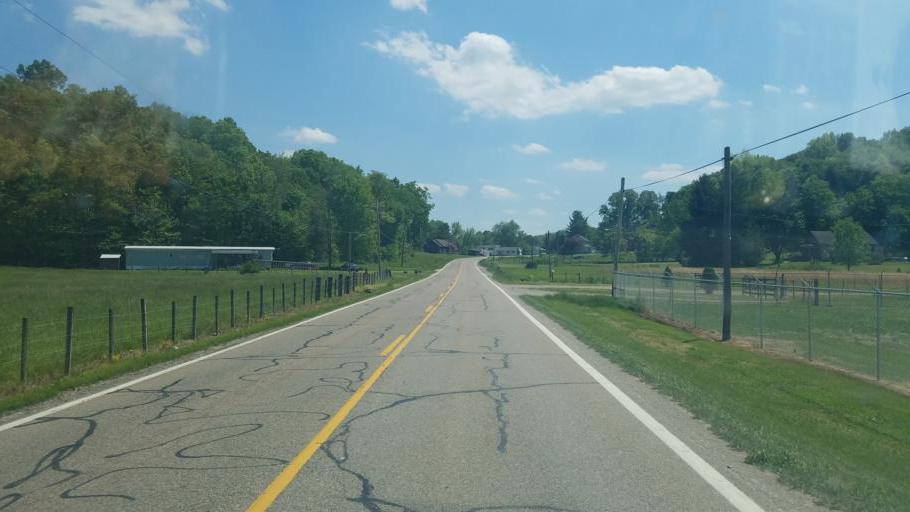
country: US
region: Ohio
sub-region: Muskingum County
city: Frazeysburg
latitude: 40.0966
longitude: -82.1683
